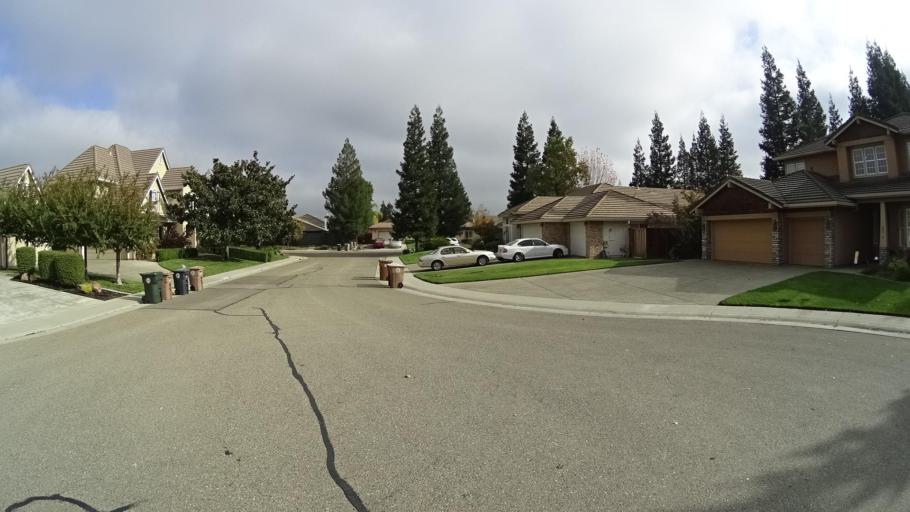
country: US
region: California
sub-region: Sacramento County
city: Elk Grove
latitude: 38.4258
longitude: -121.3656
